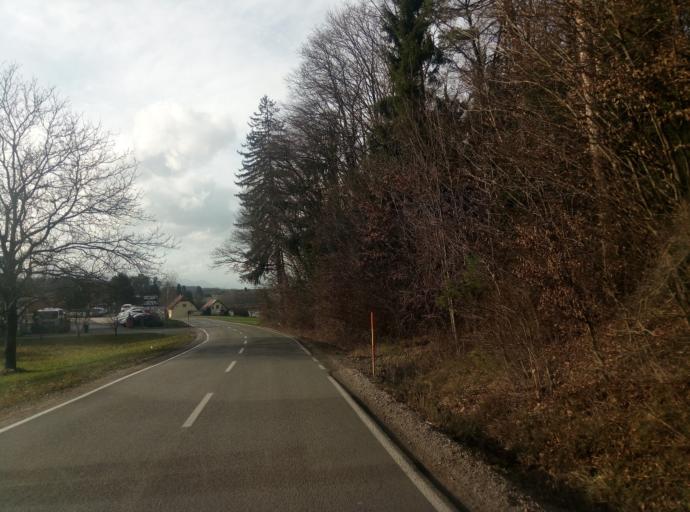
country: SI
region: Sentjur pri Celju
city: Sentjur
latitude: 46.2387
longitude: 15.3760
